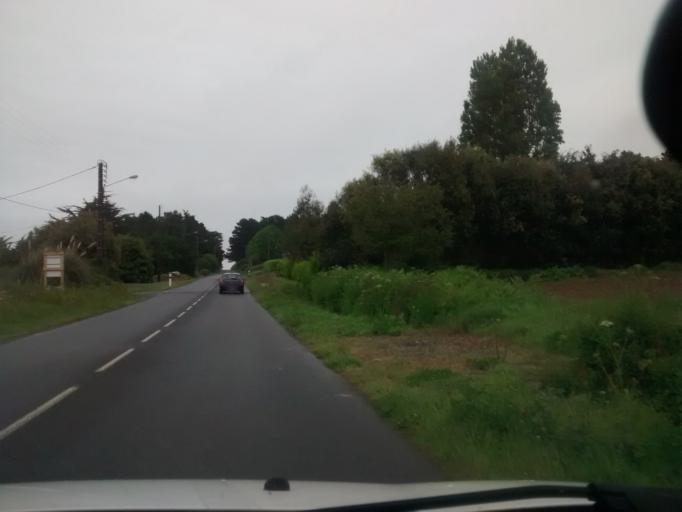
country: FR
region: Brittany
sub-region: Departement des Cotes-d'Armor
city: Trevou-Treguignec
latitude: 48.8305
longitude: -3.3190
